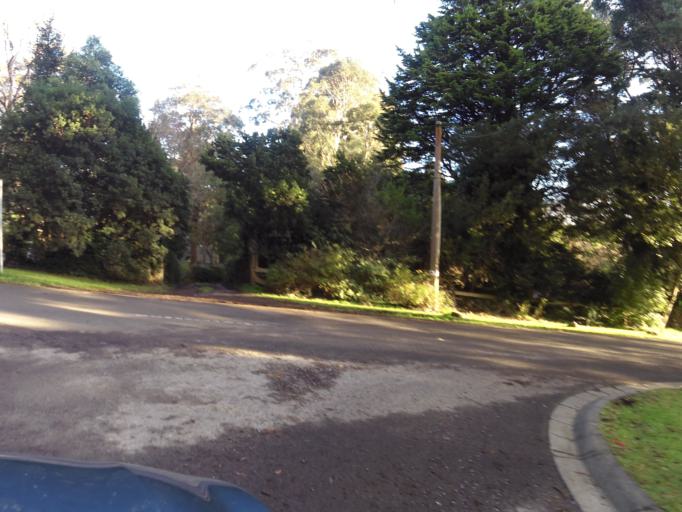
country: AU
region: Victoria
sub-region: Yarra Ranges
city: Ferny Creek
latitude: -37.8772
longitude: 145.3253
